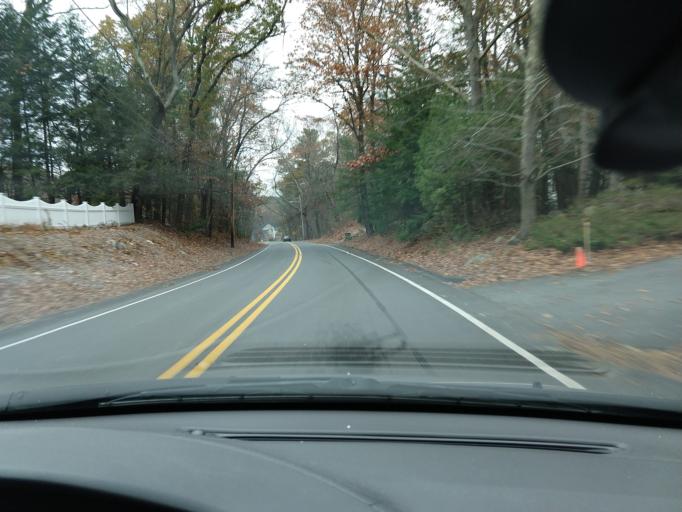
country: US
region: Massachusetts
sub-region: Middlesex County
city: Westford
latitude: 42.5922
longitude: -71.4327
